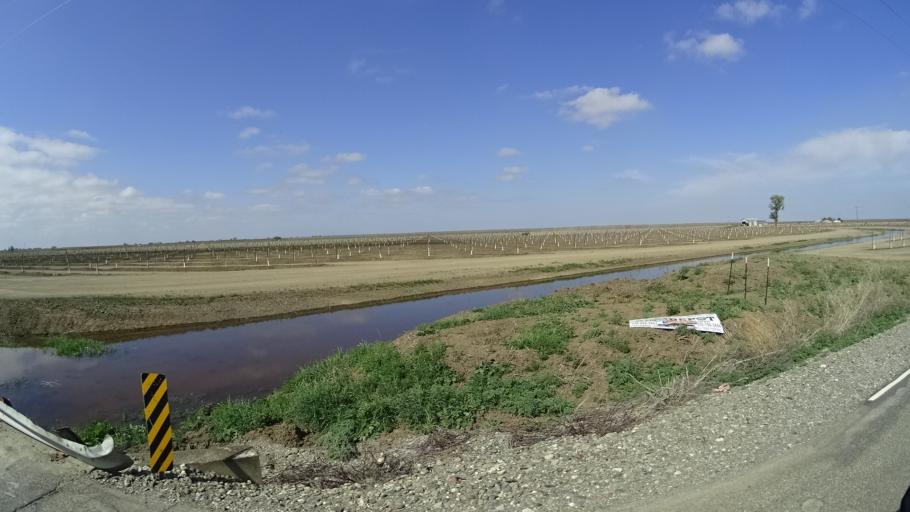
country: US
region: California
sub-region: Butte County
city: Biggs
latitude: 39.4315
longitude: -121.9296
